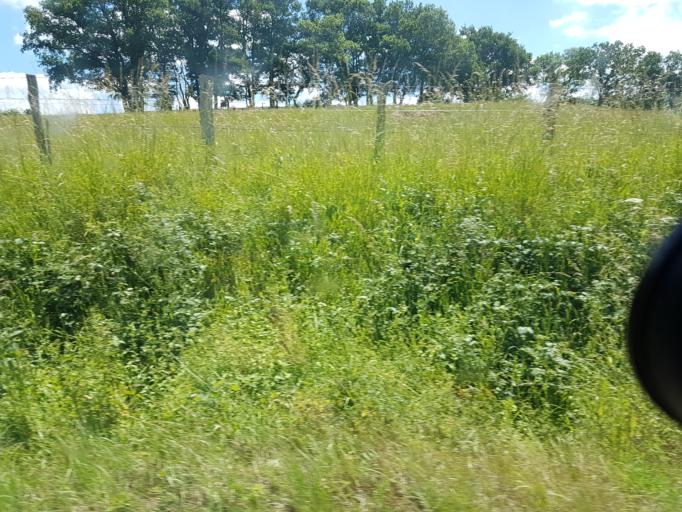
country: FR
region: Bourgogne
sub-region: Departement de Saone-et-Loire
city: Curgy
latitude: 47.0220
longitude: 4.4333
